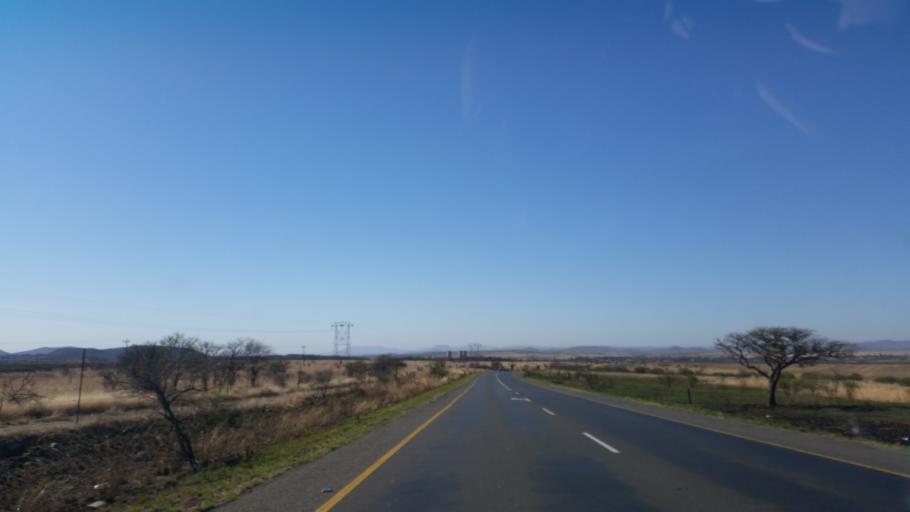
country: ZA
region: KwaZulu-Natal
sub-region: uThukela District Municipality
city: Ladysmith
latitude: -28.7122
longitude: 29.7935
